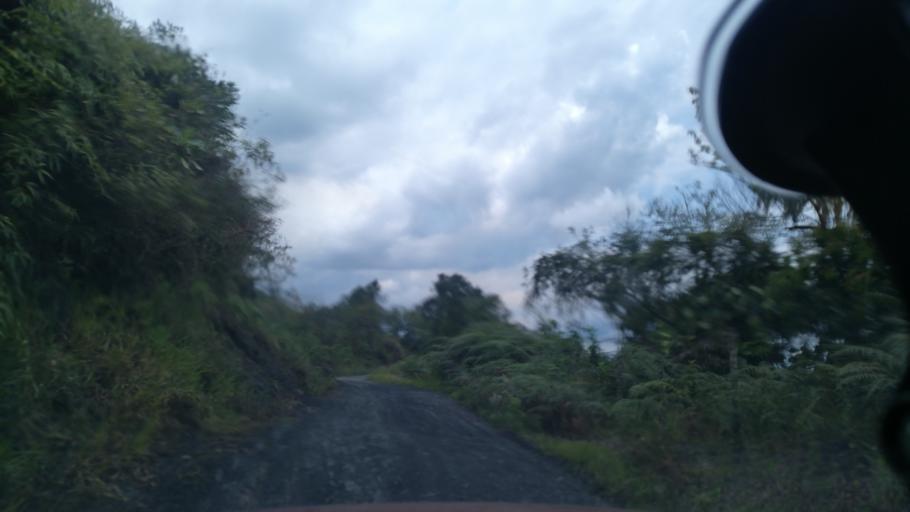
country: CO
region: Cundinamarca
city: Vergara
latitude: 5.2059
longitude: -74.2794
